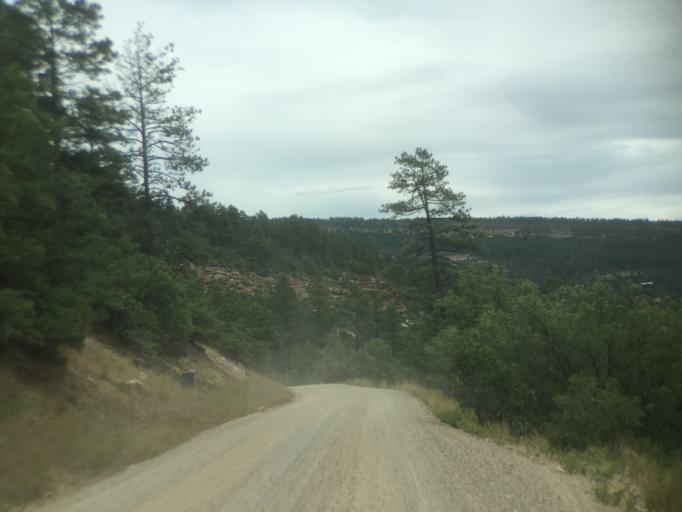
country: US
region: Colorado
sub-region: La Plata County
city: Durango
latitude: 37.3346
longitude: -107.9090
